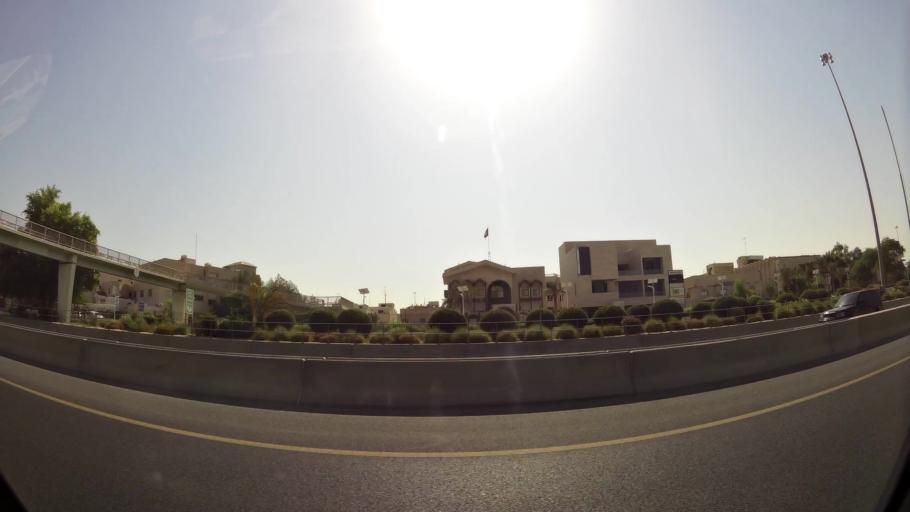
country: KW
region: Al Asimah
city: Kuwait City
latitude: 29.3624
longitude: 47.9888
